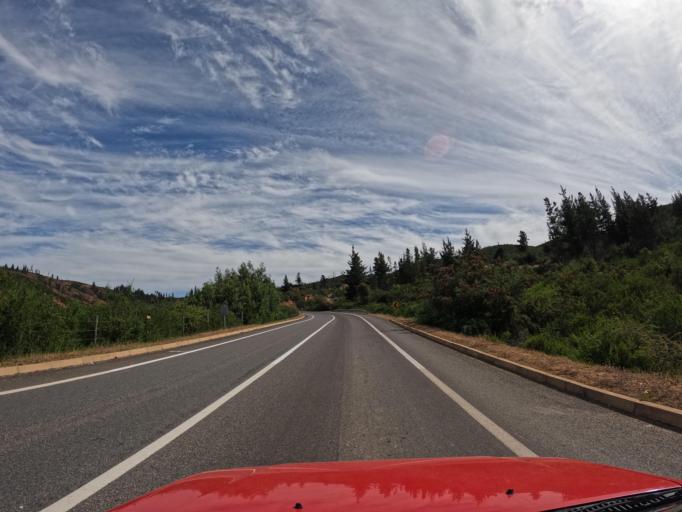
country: CL
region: Maule
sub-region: Provincia de Talca
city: Talca
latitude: -35.1594
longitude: -71.9705
